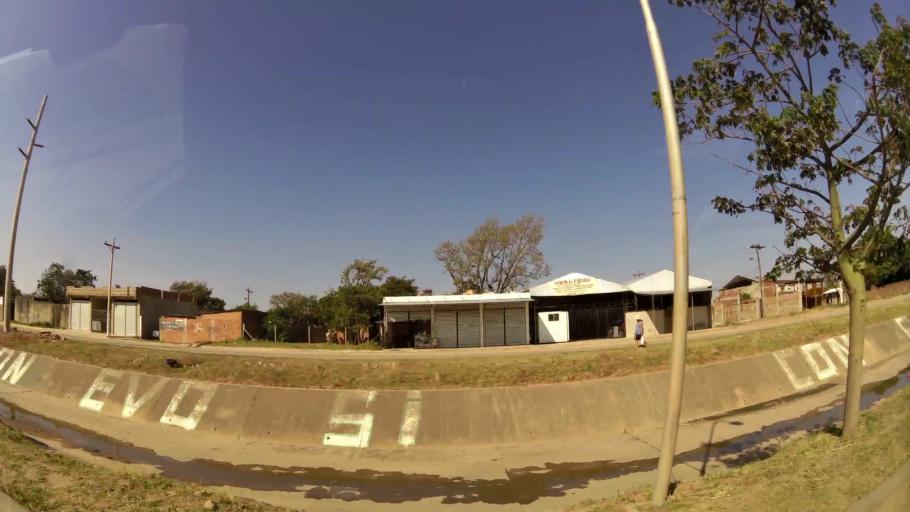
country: BO
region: Santa Cruz
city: Cotoca
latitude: -17.8110
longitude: -63.1097
